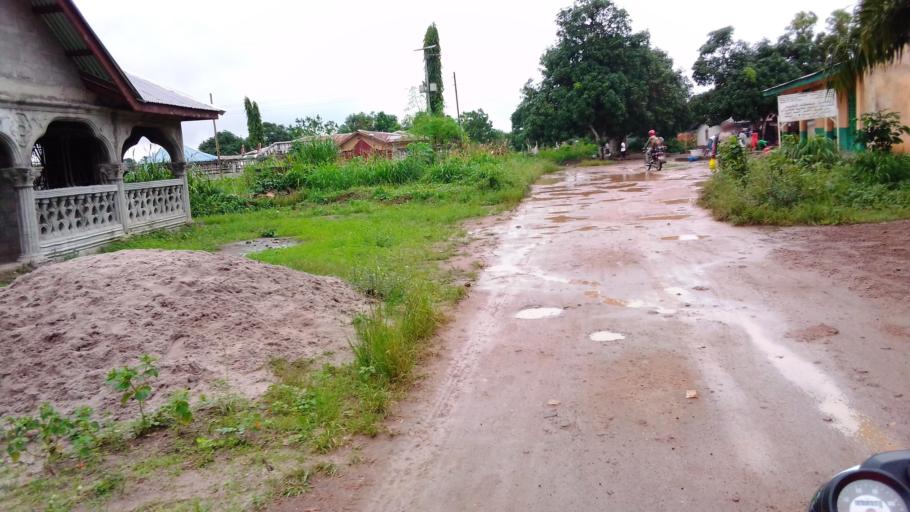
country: SL
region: Eastern Province
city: Kenema
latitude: 7.8975
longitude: -11.1680
